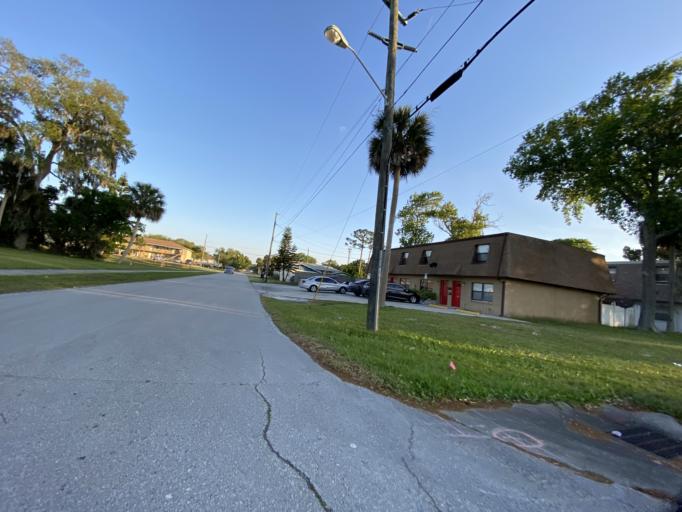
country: US
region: Florida
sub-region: Volusia County
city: South Daytona
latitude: 29.1825
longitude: -81.0095
